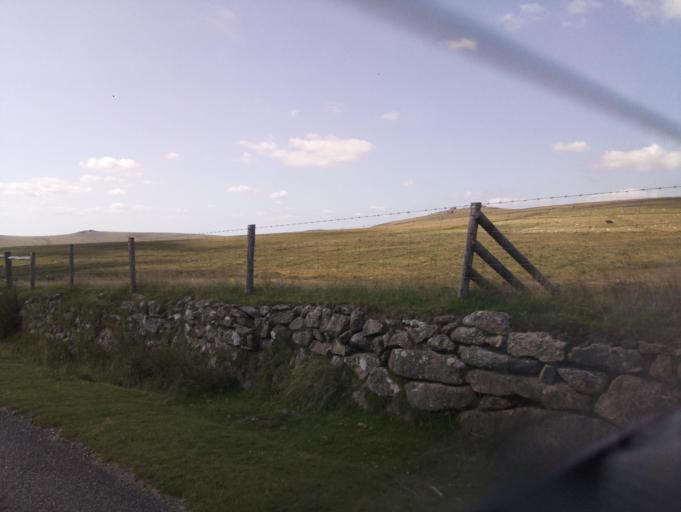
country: GB
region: England
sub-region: Devon
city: Yelverton
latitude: 50.5569
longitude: -4.0208
